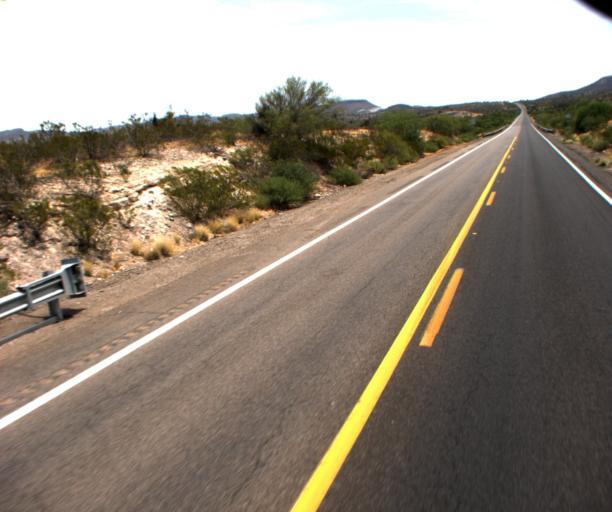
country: US
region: Arizona
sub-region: Gila County
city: Peridot
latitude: 33.2884
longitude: -110.3965
